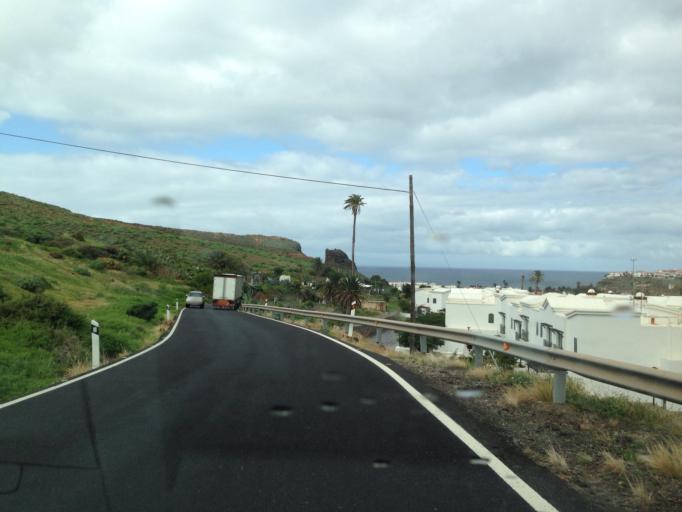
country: ES
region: Canary Islands
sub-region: Provincia de Las Palmas
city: Agaete
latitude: 28.0970
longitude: -15.7014
